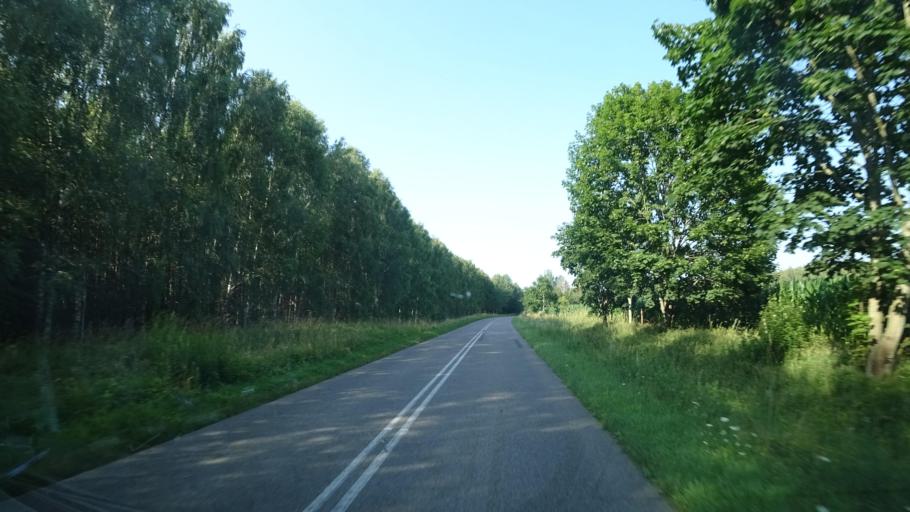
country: PL
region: Pomeranian Voivodeship
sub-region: Powiat czluchowski
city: Rzeczenica
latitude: 53.7852
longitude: 17.1678
